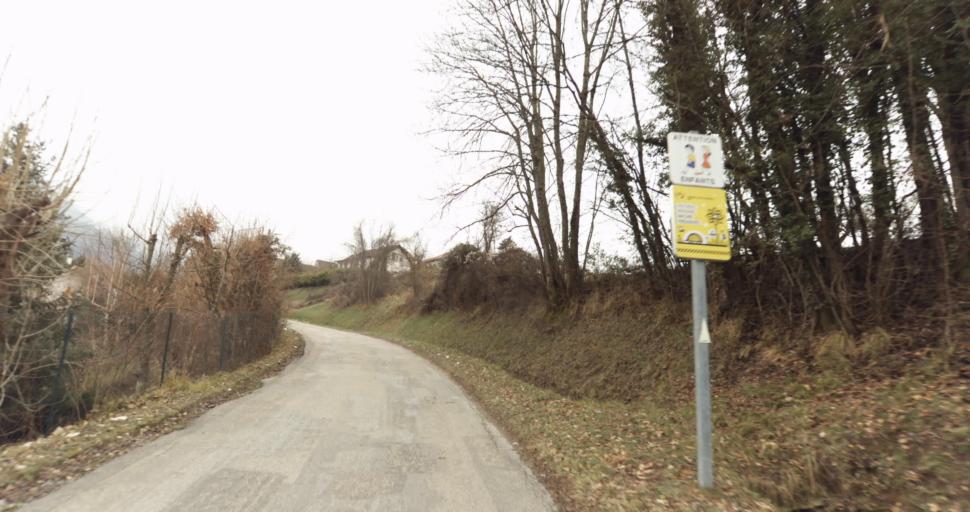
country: FR
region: Rhone-Alpes
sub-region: Departement de l'Isere
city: Vif
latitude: 45.0224
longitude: 5.6563
